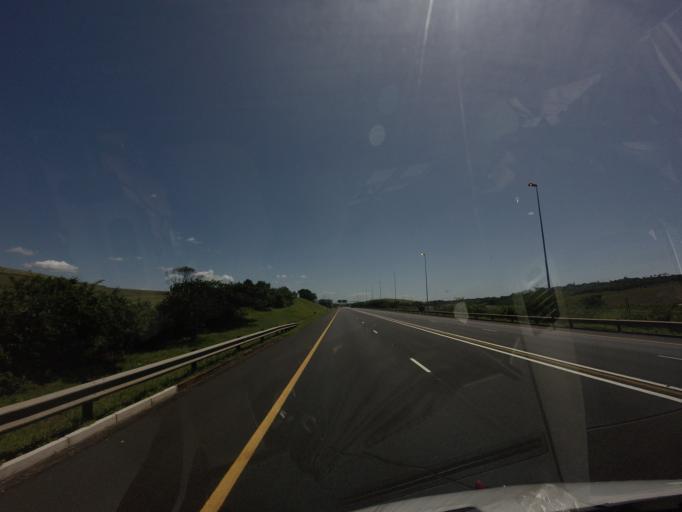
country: ZA
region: KwaZulu-Natal
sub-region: uThungulu District Municipality
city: eSikhawini
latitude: -28.9601
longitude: 31.7358
